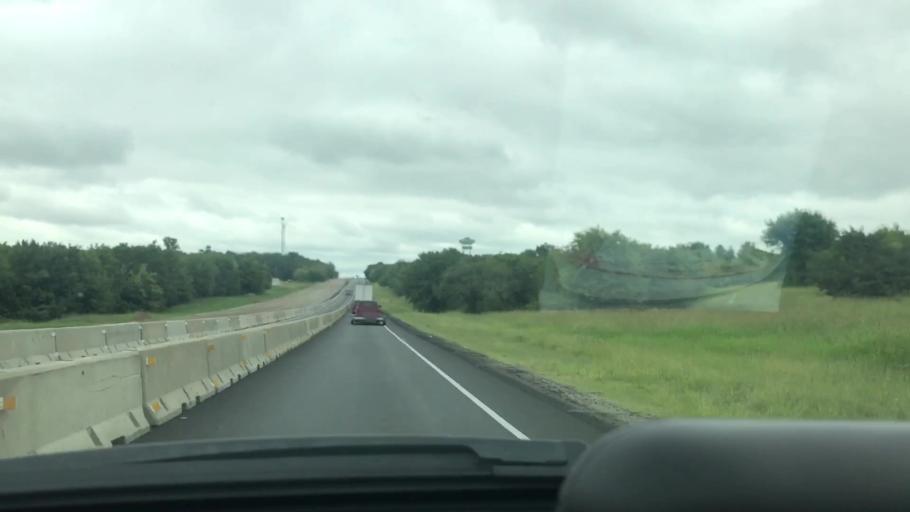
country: US
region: Oklahoma
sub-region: McIntosh County
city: Eufaula
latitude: 35.2789
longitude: -95.5931
